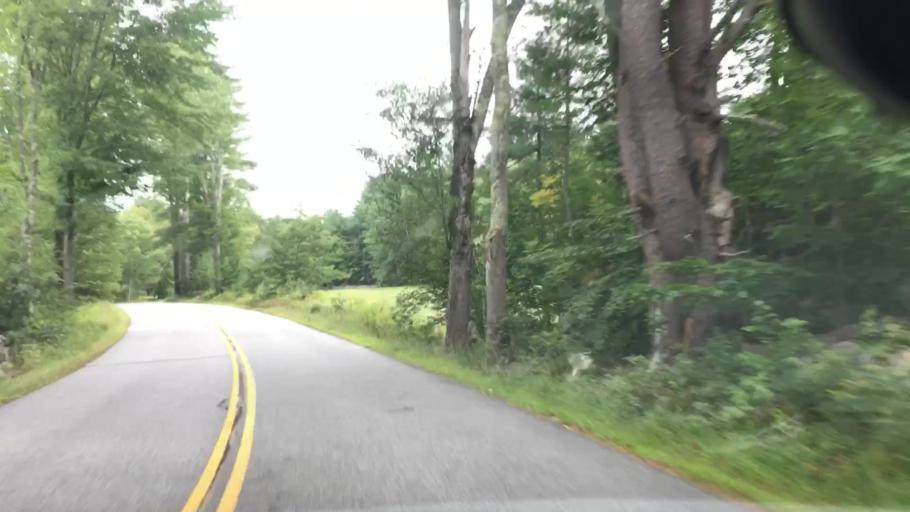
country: US
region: New Hampshire
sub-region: Hillsborough County
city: Milford
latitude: 42.8513
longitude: -71.5751
